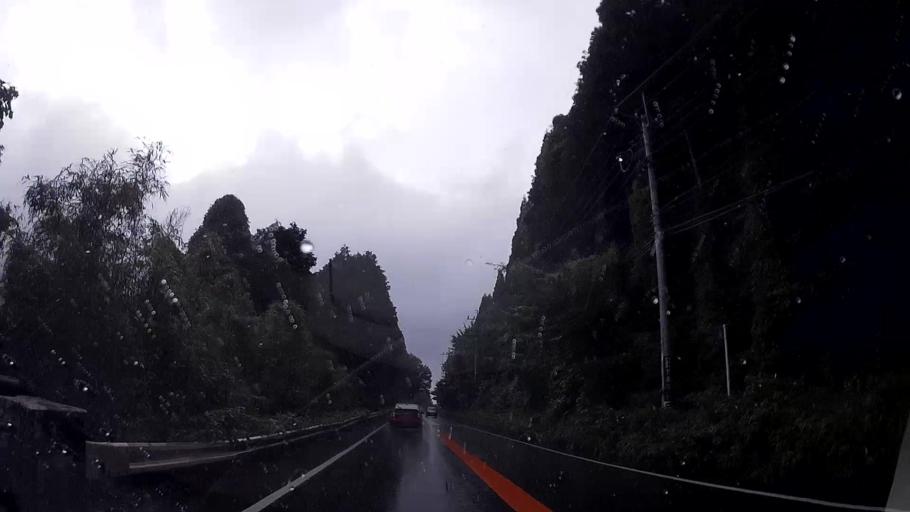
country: JP
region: Kumamoto
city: Aso
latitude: 32.8690
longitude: 130.9983
